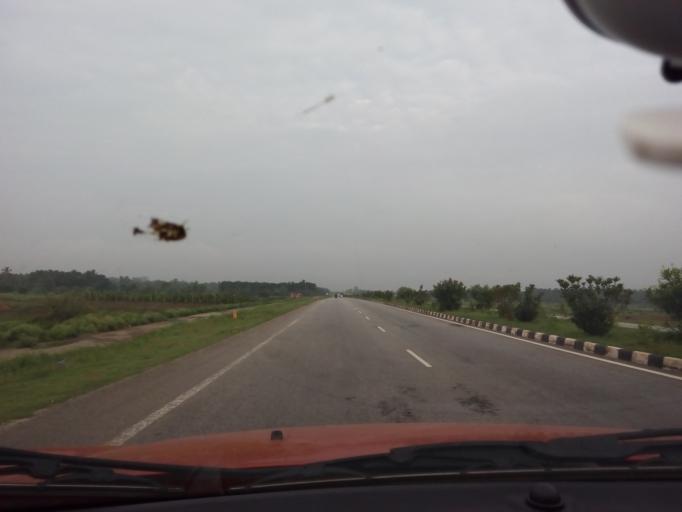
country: IN
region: Karnataka
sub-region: Tumkur
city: Kunigal
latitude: 13.0050
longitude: 77.0014
